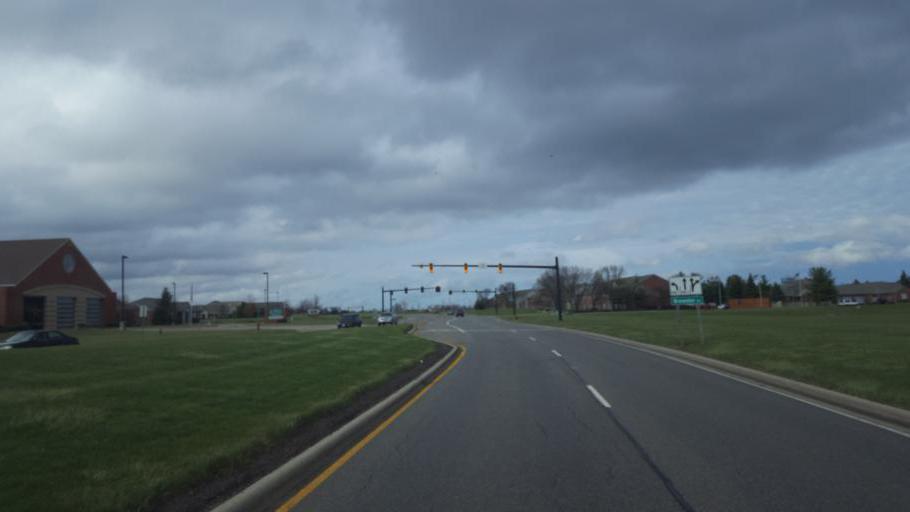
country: US
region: Ohio
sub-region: Delaware County
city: Powell
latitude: 40.1499
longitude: -83.0926
